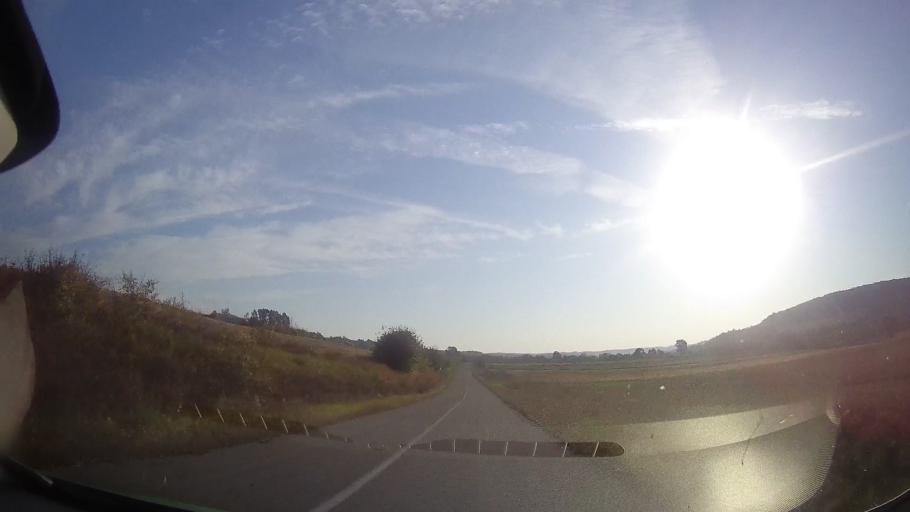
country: RO
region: Timis
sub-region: Comuna Bogda
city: Bogda
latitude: 45.9821
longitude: 21.5438
